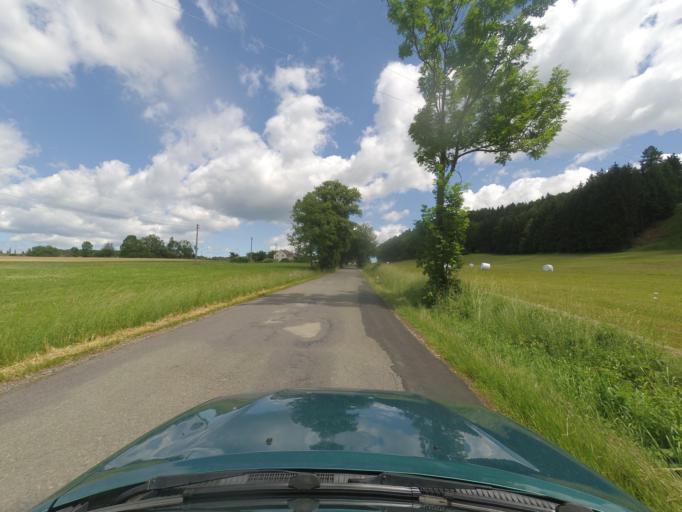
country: CZ
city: Rokytnice v Orlickych Horach
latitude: 50.1275
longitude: 16.4201
